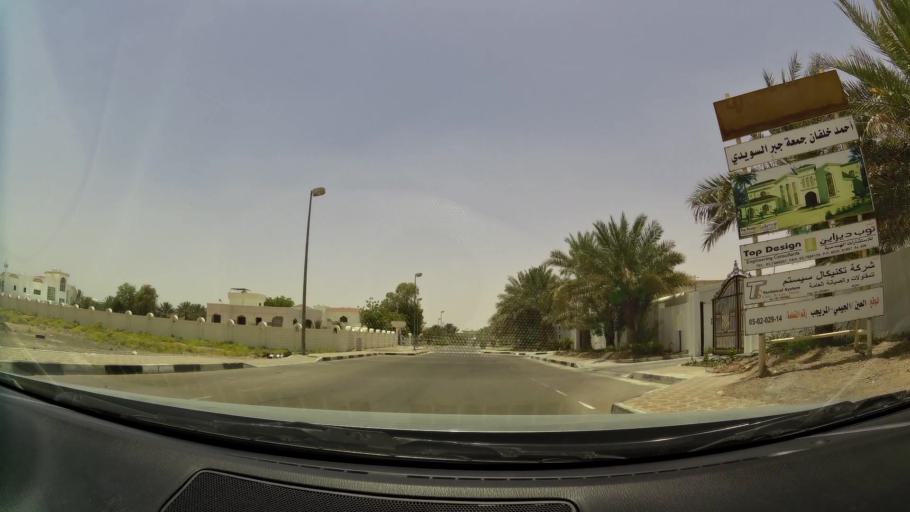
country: OM
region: Al Buraimi
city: Al Buraymi
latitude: 24.2637
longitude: 55.7252
